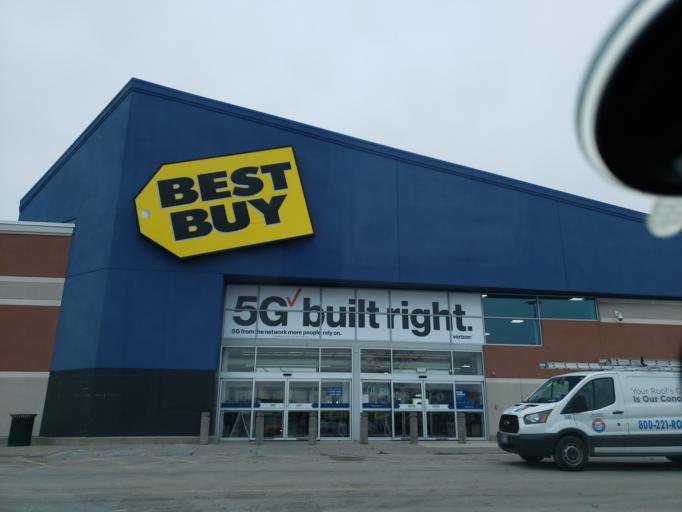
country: US
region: Illinois
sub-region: Cook County
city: Orland Hills
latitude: 41.6019
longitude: -87.8563
